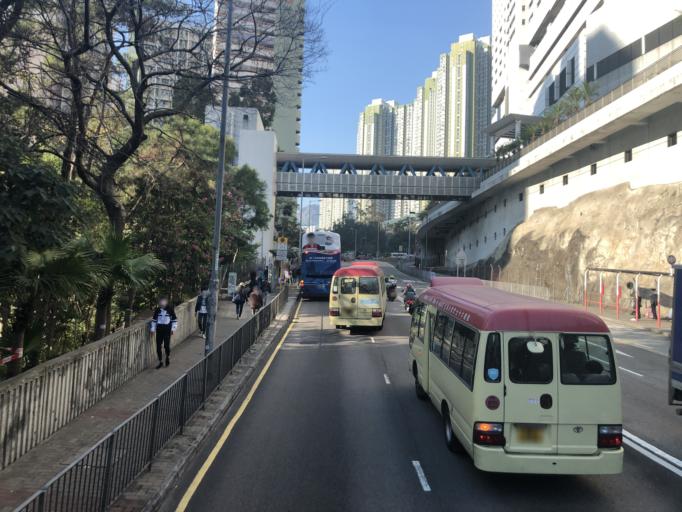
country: HK
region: Kowloon City
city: Kowloon
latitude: 22.3165
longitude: 114.2361
